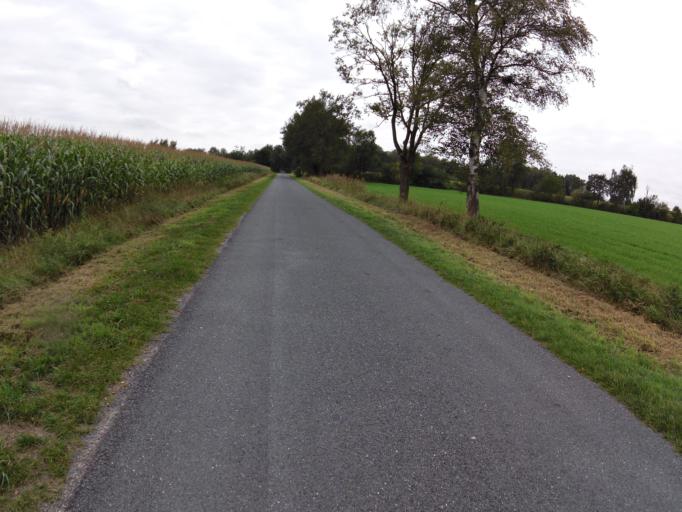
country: DE
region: Lower Saxony
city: Bad Bentheim
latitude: 52.2672
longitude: 7.1181
